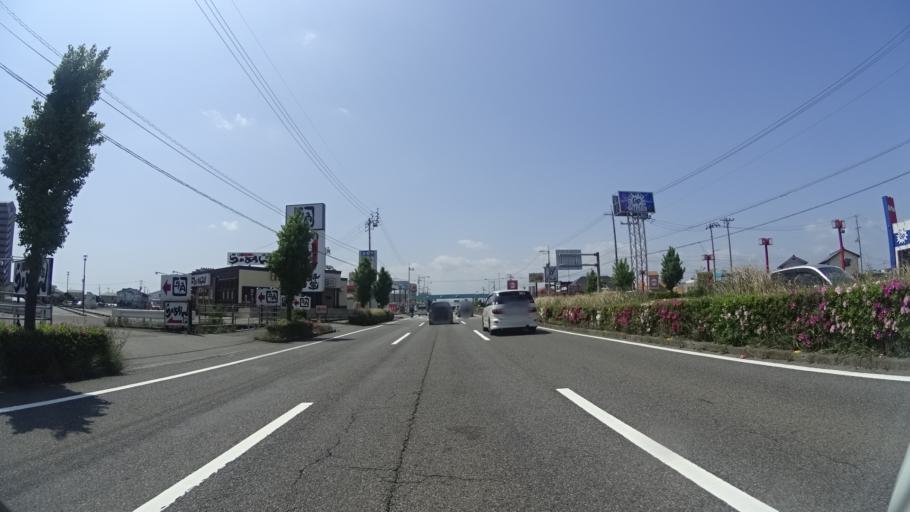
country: JP
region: Tokushima
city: Tokushima-shi
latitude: 34.1138
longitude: 134.5776
